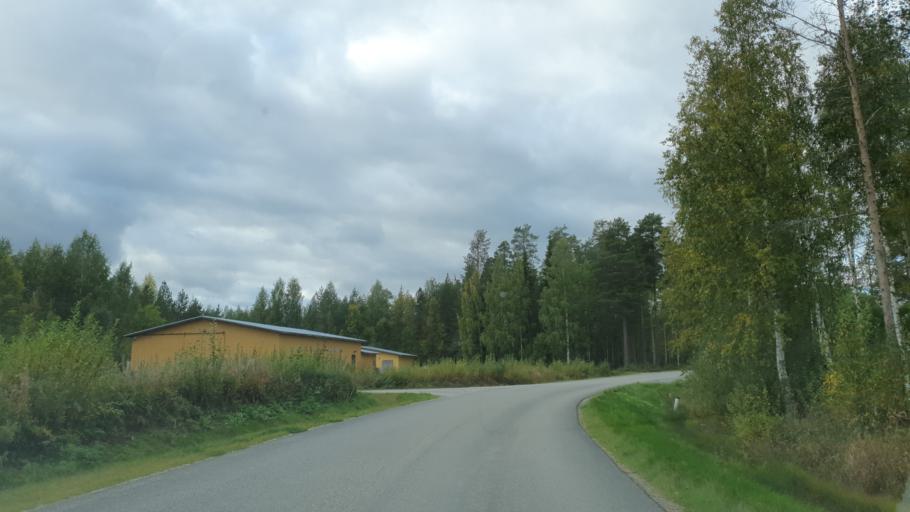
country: FI
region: Kainuu
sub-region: Kehys-Kainuu
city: Kuhmo
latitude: 64.1096
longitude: 29.4913
